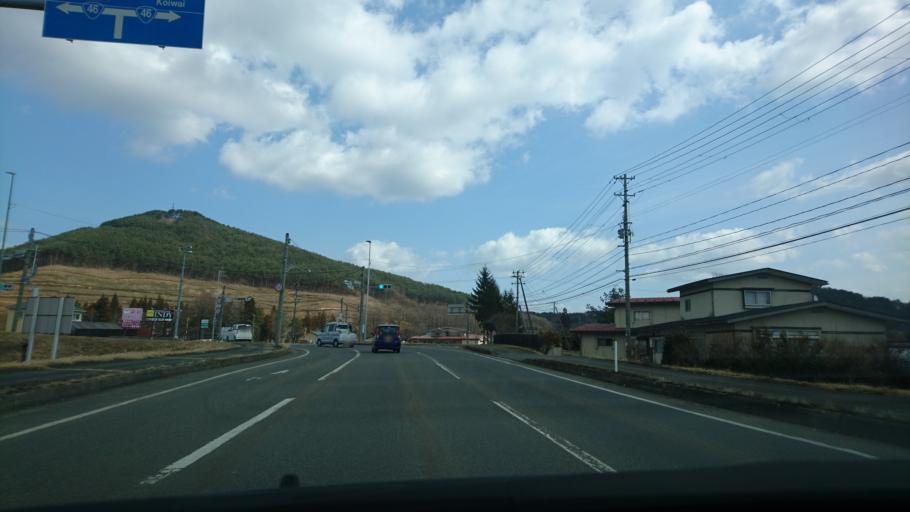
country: JP
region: Iwate
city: Shizukuishi
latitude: 39.6890
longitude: 140.9918
